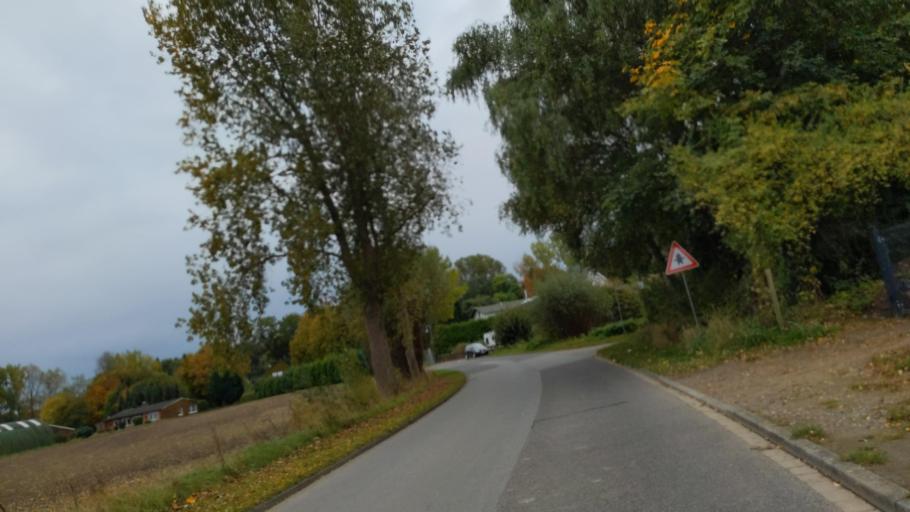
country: DE
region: Schleswig-Holstein
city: Scharbeutz
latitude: 54.0404
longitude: 10.7238
